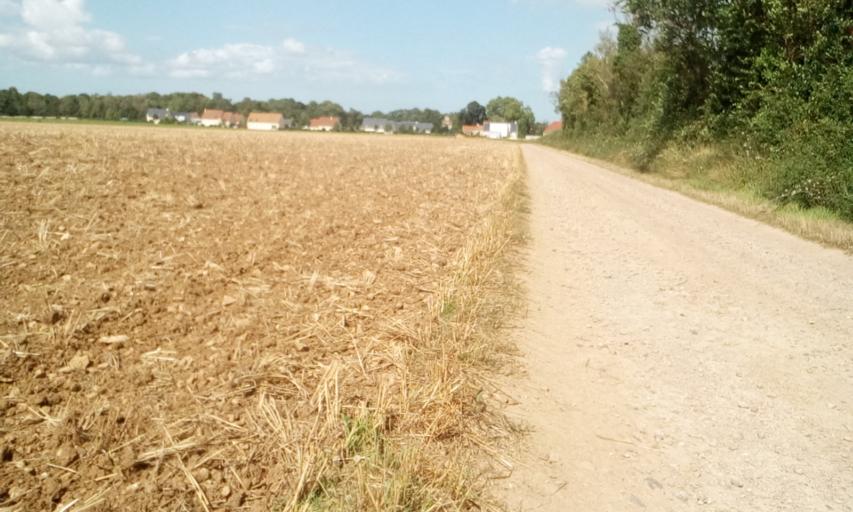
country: FR
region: Lower Normandy
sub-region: Departement du Calvados
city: Bellengreville
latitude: 49.1069
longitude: -0.2257
